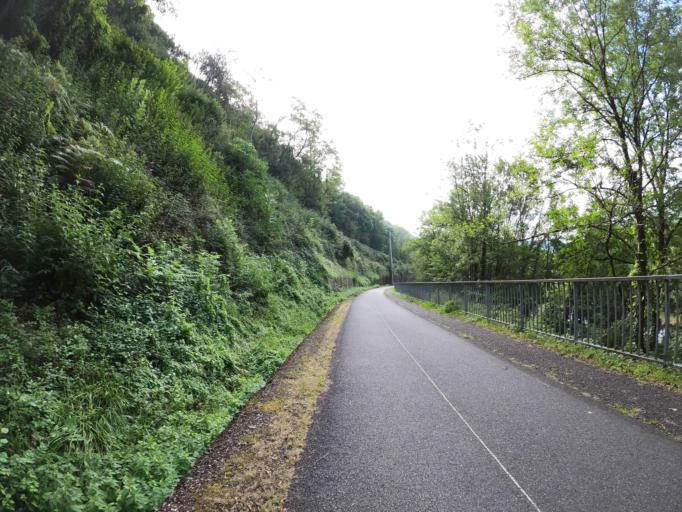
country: FR
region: Midi-Pyrenees
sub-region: Departement des Hautes-Pyrenees
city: Lourdes
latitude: 43.0808
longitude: -0.0419
